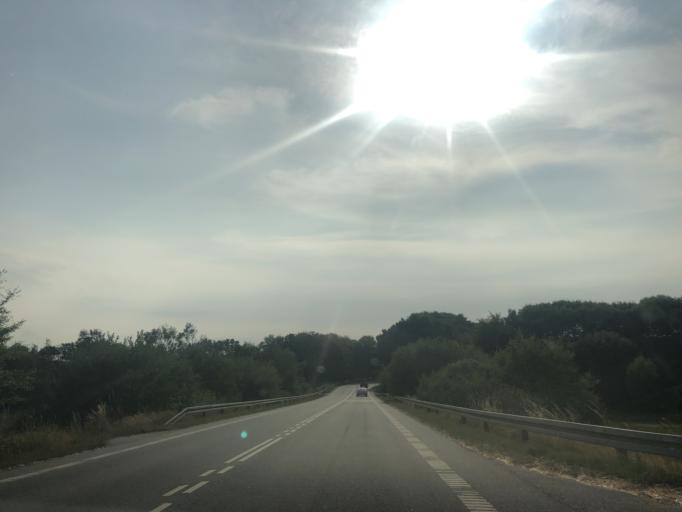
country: DK
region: Central Jutland
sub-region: Skive Kommune
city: Skive
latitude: 56.6276
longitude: 8.9027
